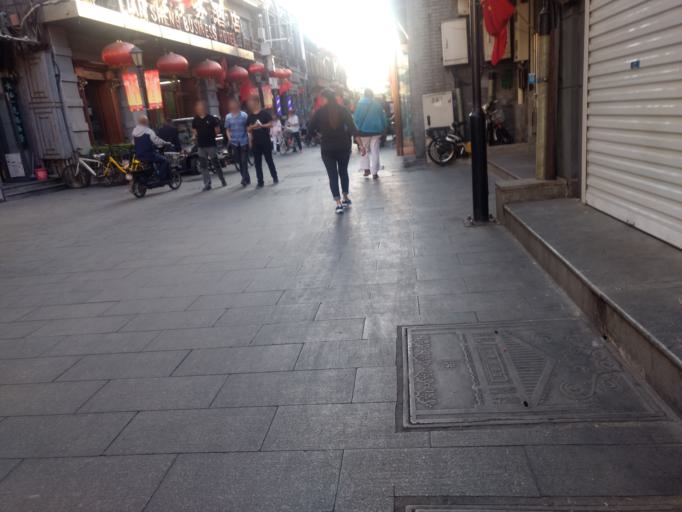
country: CN
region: Beijing
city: Beijing
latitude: 39.8940
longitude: 116.3875
